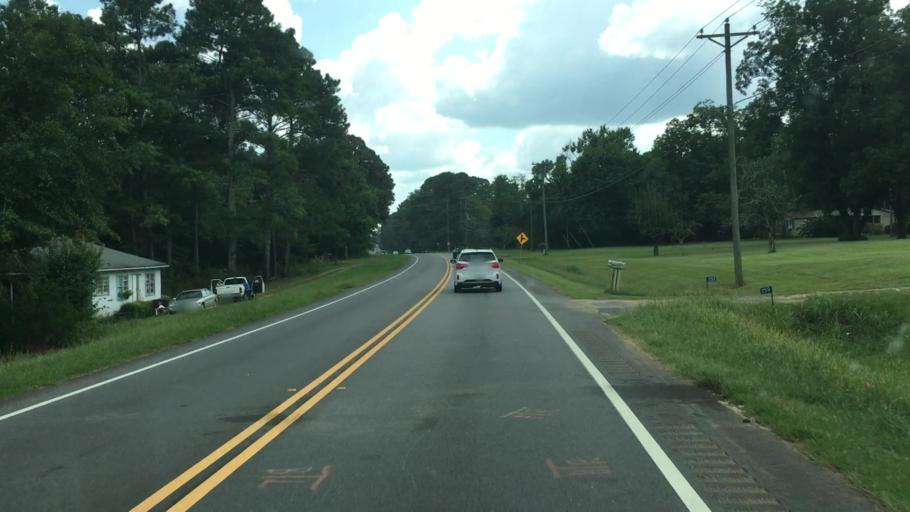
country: US
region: Georgia
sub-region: Putnam County
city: Eatonton
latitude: 33.3568
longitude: -83.3897
